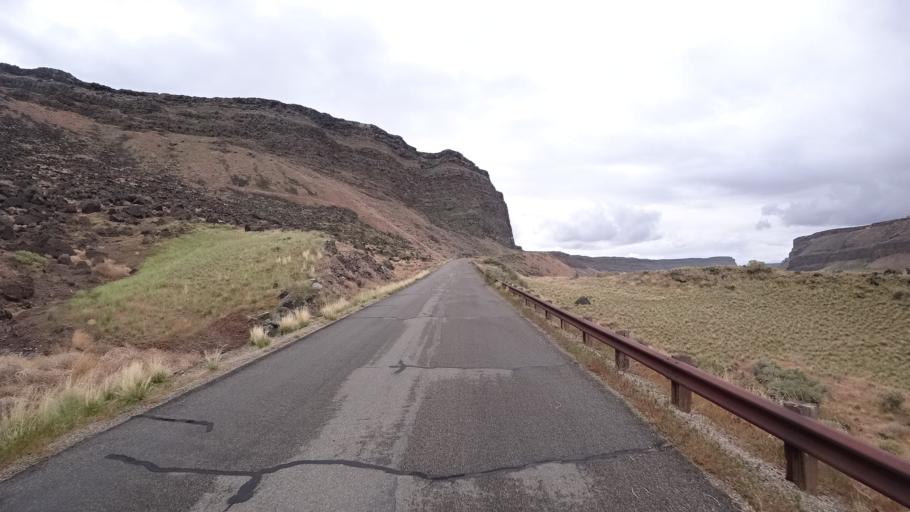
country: US
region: Idaho
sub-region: Owyhee County
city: Murphy
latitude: 43.2489
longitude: -116.3756
